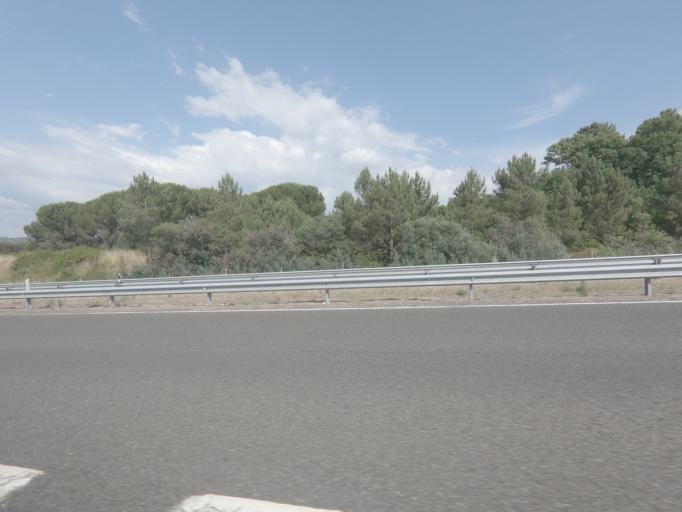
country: ES
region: Galicia
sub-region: Provincia de Ourense
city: Ourense
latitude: 42.2994
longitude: -7.8758
